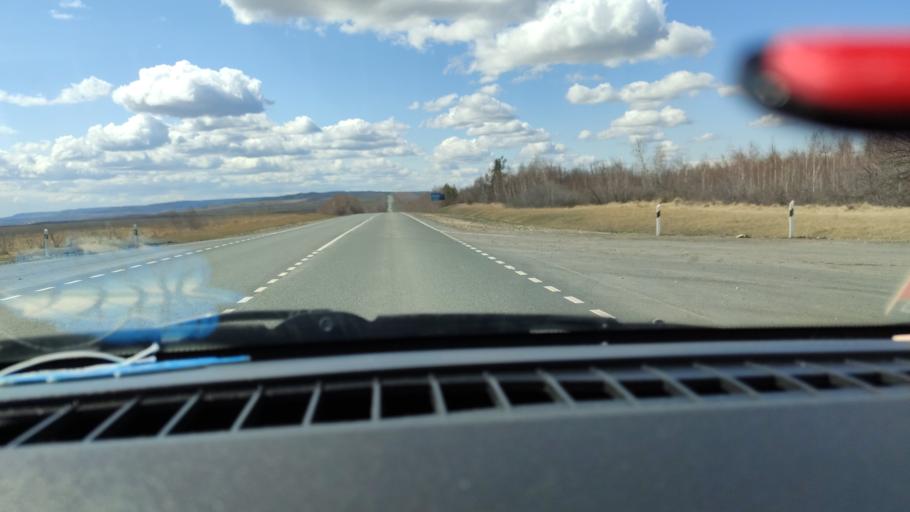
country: RU
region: Saratov
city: Khvalynsk
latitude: 52.5835
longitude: 48.1202
